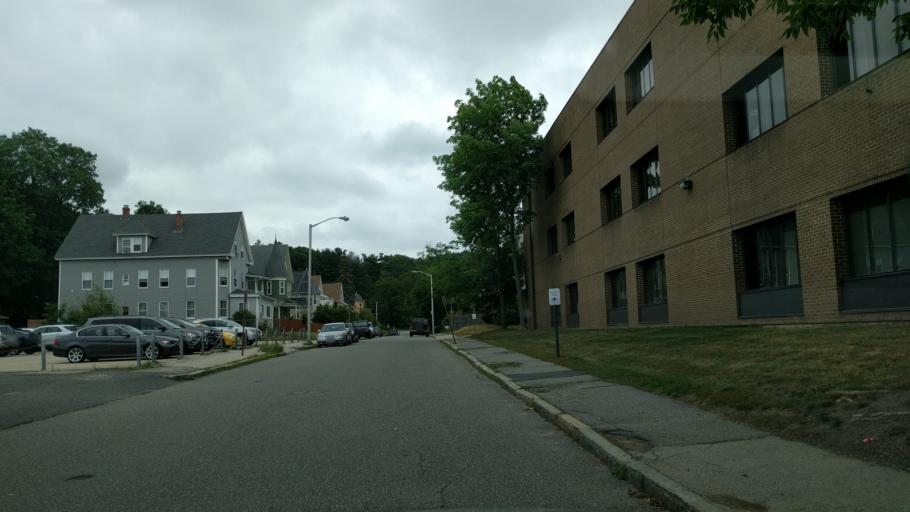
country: US
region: Massachusetts
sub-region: Worcester County
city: Worcester
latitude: 42.2862
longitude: -71.7895
